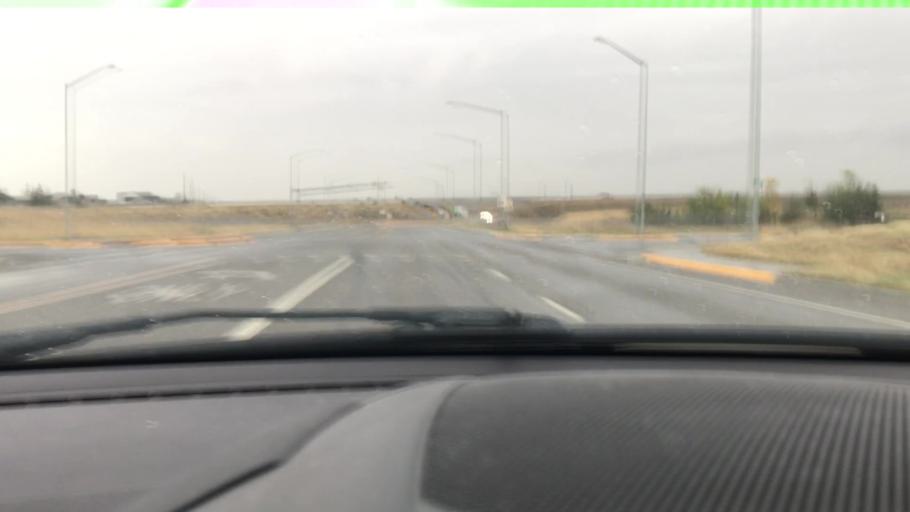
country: US
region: Montana
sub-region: Gallatin County
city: Belgrade
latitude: 45.7573
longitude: -111.1642
